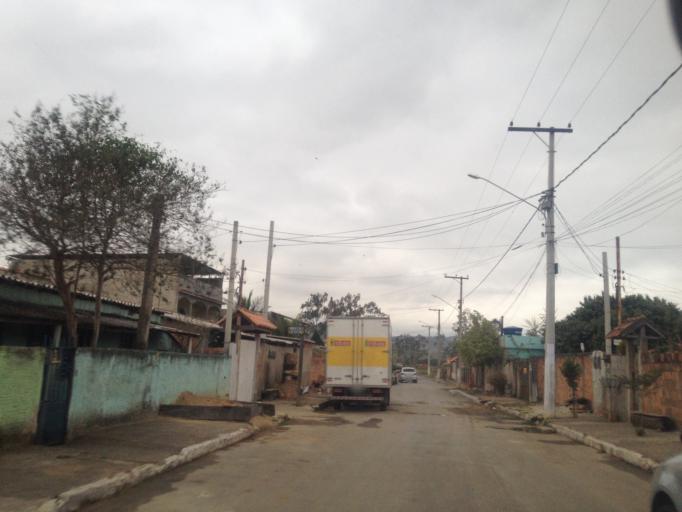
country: BR
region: Rio de Janeiro
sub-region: Porto Real
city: Porto Real
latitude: -22.4088
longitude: -44.2976
